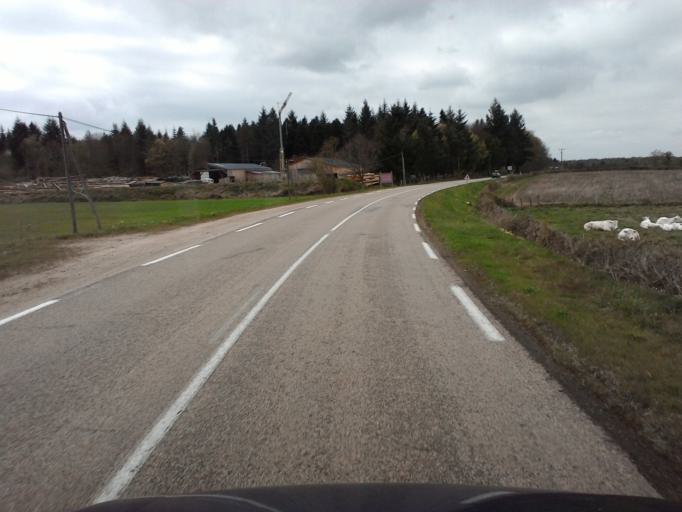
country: FR
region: Bourgogne
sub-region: Departement de l'Yonne
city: Avallon
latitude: 47.3331
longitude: 4.0249
